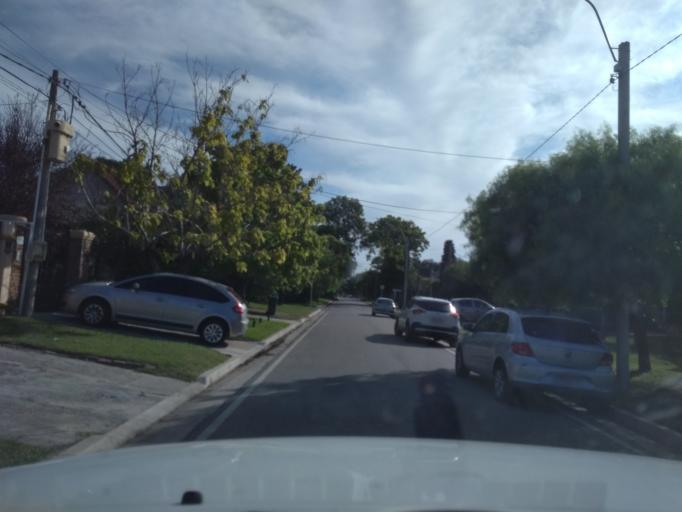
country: UY
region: Canelones
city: Barra de Carrasco
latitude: -34.8670
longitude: -56.0334
